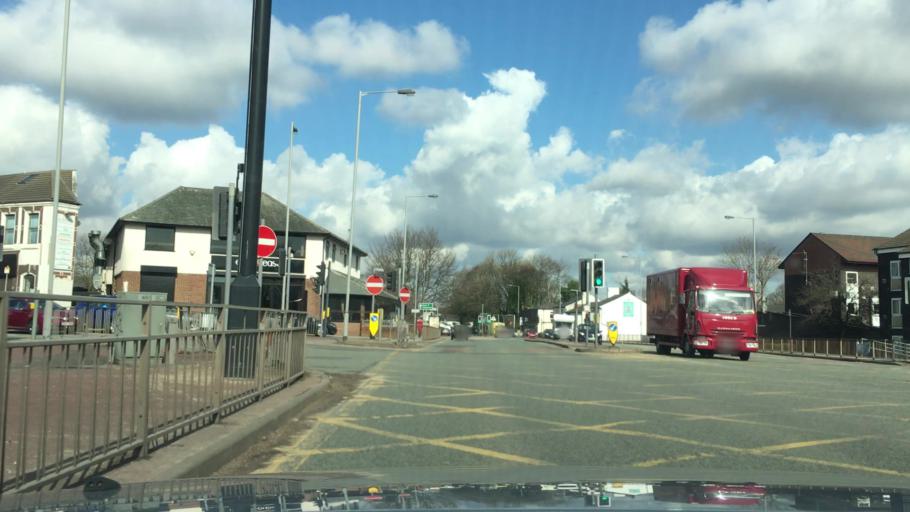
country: GB
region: England
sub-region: Borough of Bury
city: Whitefield
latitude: 53.5436
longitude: -2.2908
